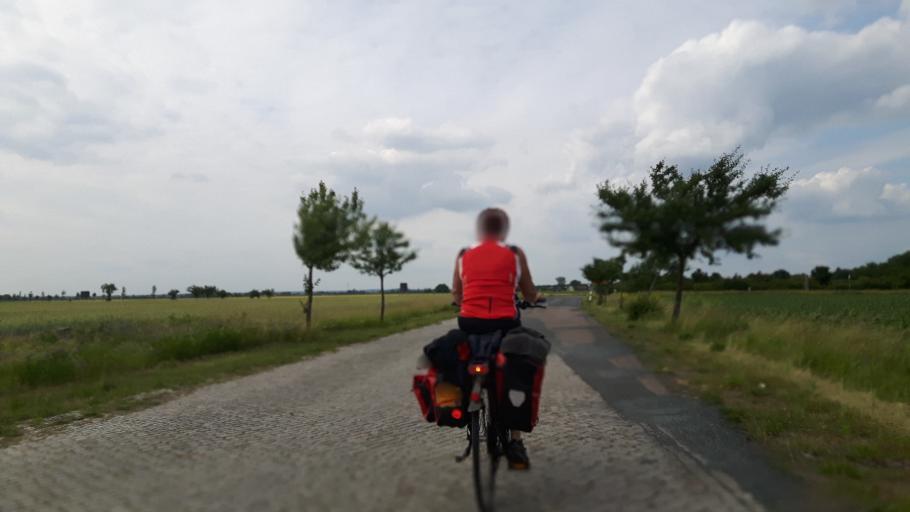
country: DE
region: Saxony-Anhalt
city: Bergwitz
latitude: 51.8079
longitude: 12.5727
